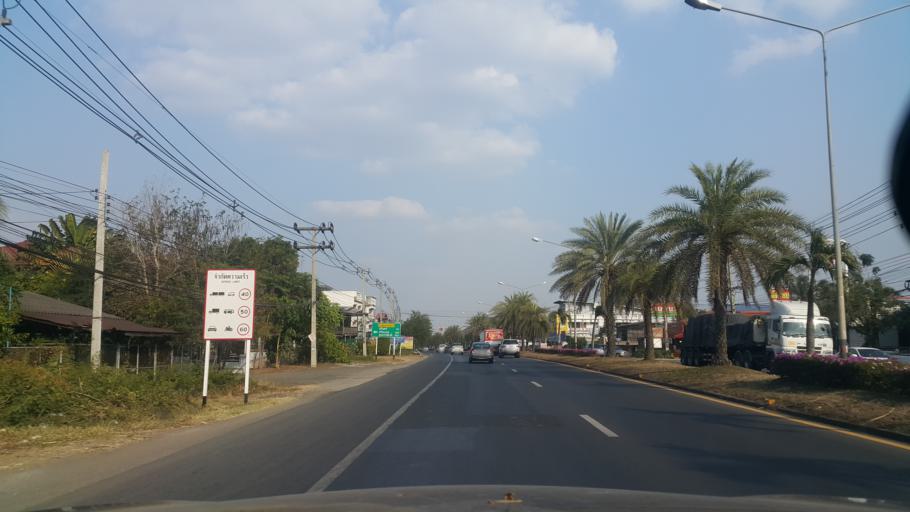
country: TH
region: Buriram
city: Nang Rong
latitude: 14.6323
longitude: 102.8194
